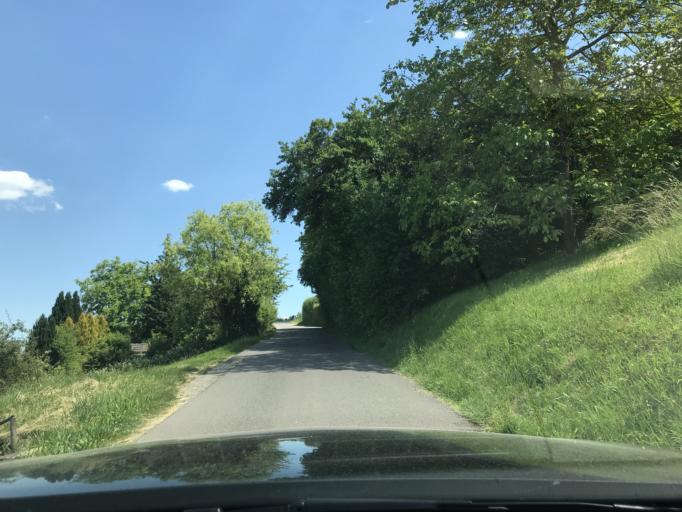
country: DE
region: Baden-Wuerttemberg
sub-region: Regierungsbezirk Stuttgart
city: Weinstadt-Endersbach
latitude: 48.7951
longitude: 9.3809
